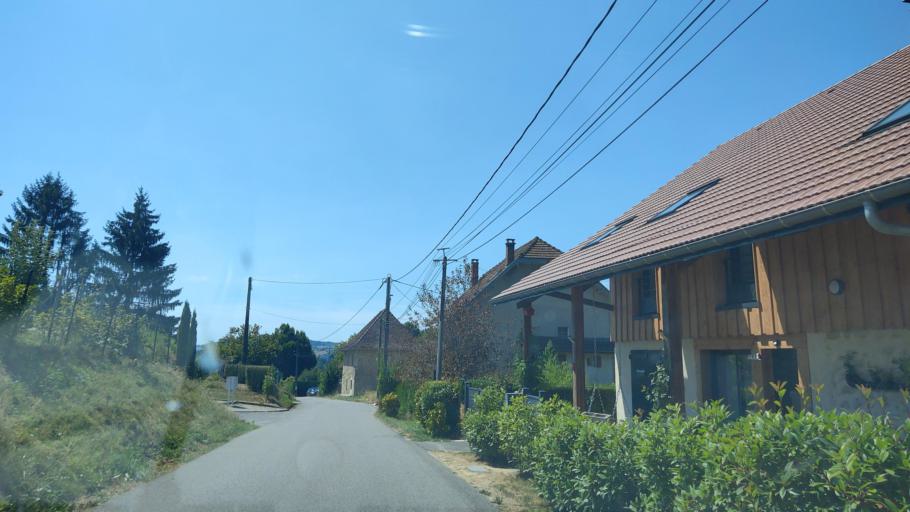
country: FR
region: Rhone-Alpes
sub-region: Departement de la Savoie
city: Novalaise
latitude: 45.5935
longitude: 5.7919
